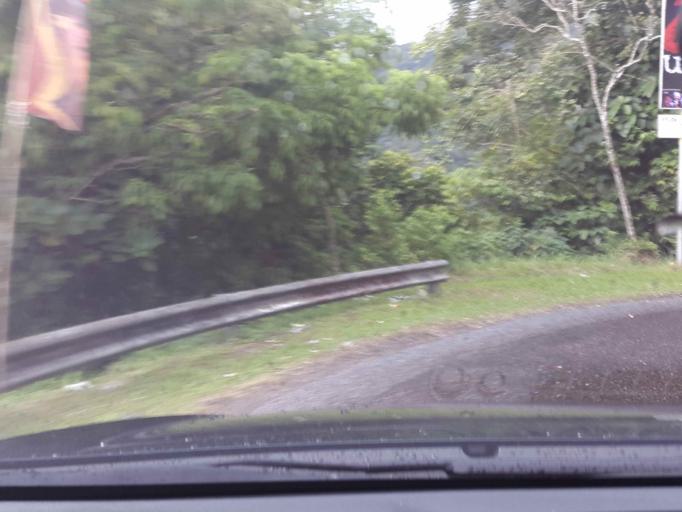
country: ID
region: West Sumatra
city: Maninjau
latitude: -0.3006
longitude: 100.2331
